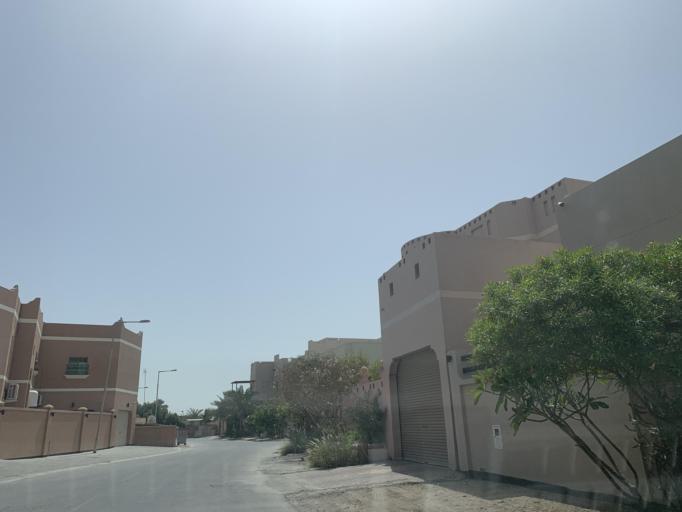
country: BH
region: Northern
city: Sitrah
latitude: 26.1543
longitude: 50.5859
